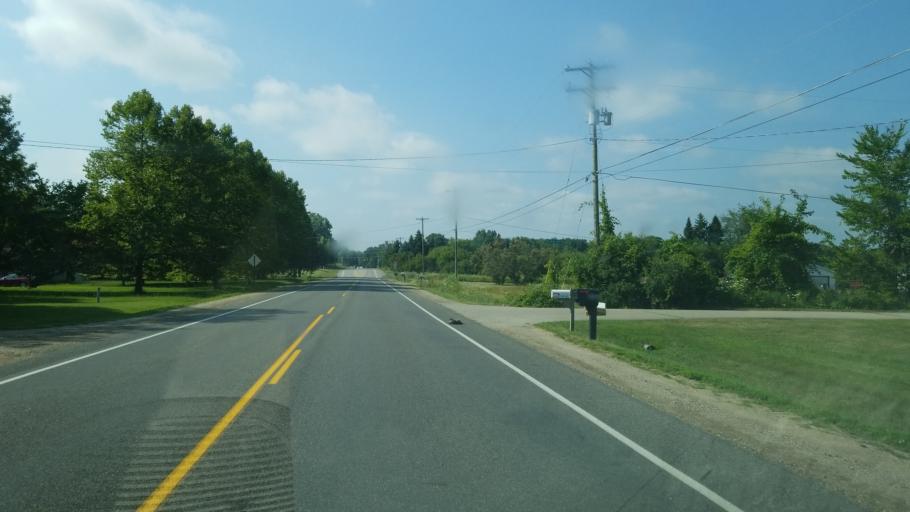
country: US
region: Michigan
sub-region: Kent County
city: Northview
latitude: 43.0989
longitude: -85.6390
